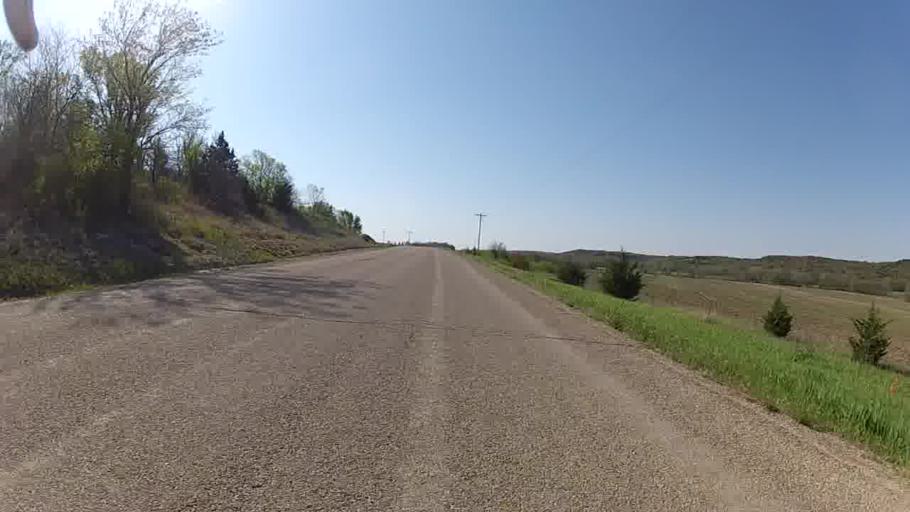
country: US
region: Kansas
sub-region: Riley County
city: Ogden
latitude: 39.0423
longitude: -96.7177
